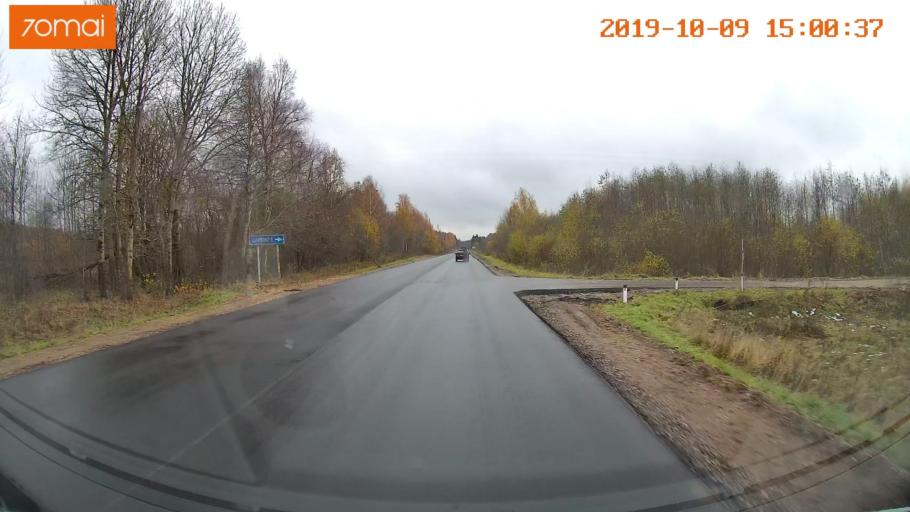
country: RU
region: Kostroma
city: Chistyye Bory
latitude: 58.3073
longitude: 41.6785
